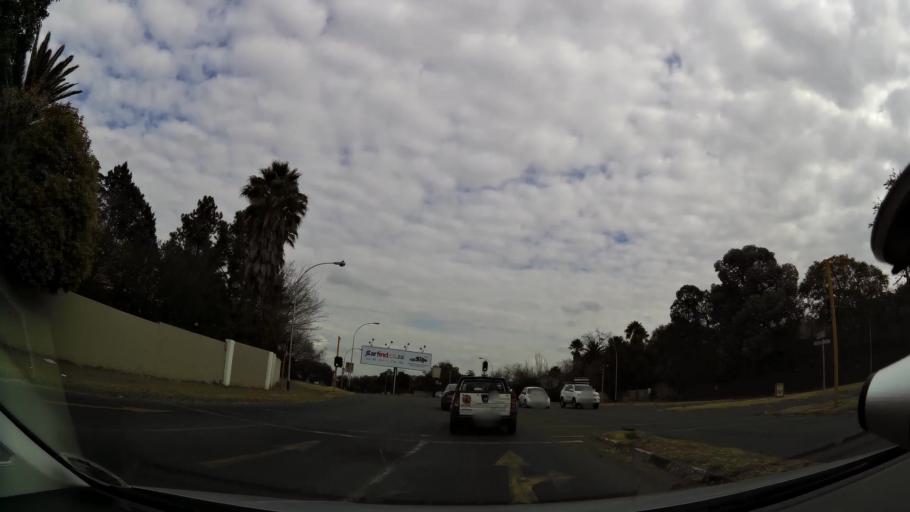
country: ZA
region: Orange Free State
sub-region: Mangaung Metropolitan Municipality
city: Bloemfontein
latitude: -29.0982
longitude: 26.2234
